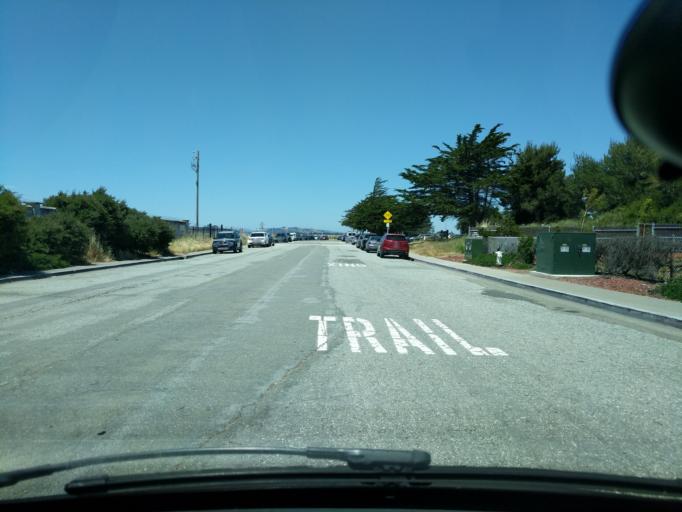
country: US
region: California
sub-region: Contra Costa County
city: El Cerrito
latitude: 37.8977
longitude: -122.3231
